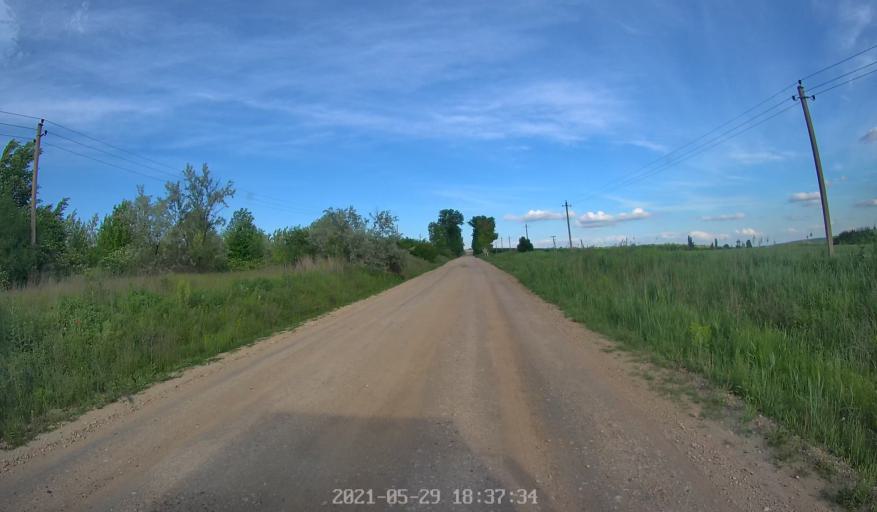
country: MD
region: Chisinau
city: Singera
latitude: 46.8039
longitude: 28.9318
